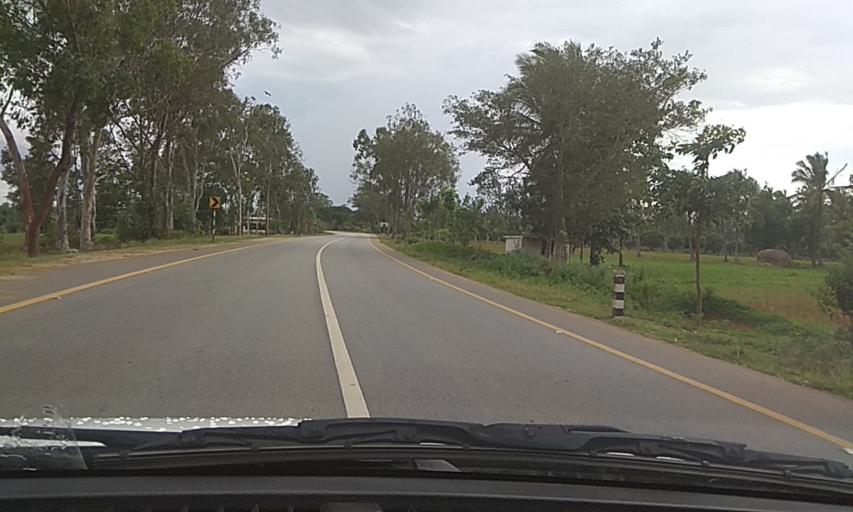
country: IN
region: Karnataka
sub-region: Tumkur
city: Kunigal
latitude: 12.9173
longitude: 77.0325
